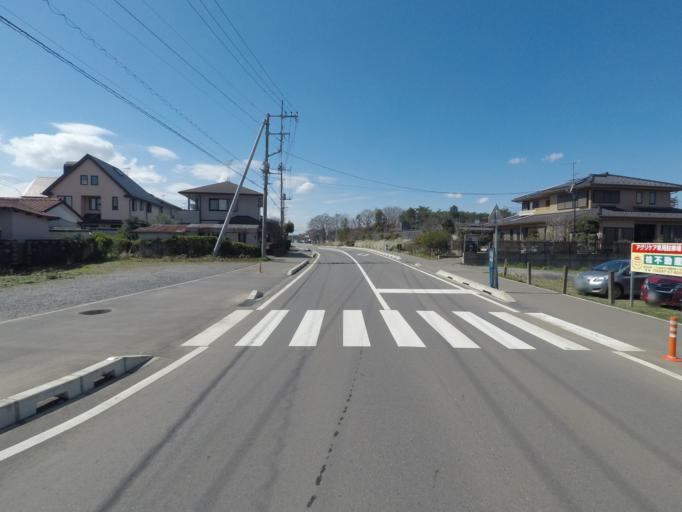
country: JP
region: Ibaraki
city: Mitsukaido
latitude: 35.9912
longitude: 140.0574
